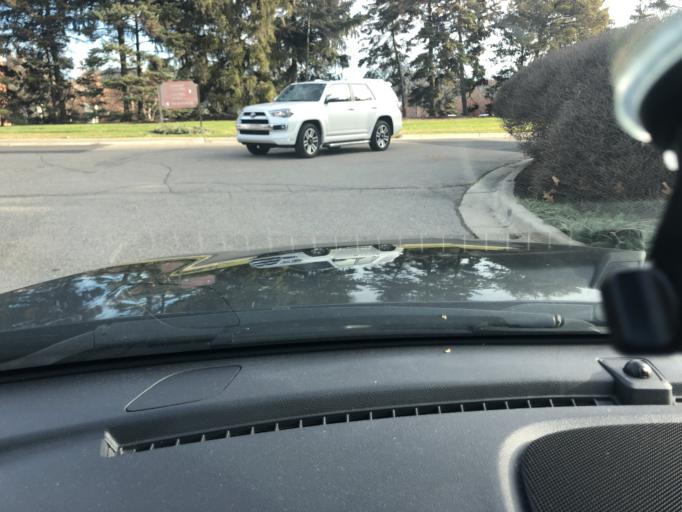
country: US
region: Michigan
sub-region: Wayne County
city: Allen Park
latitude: 42.2973
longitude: -83.2304
